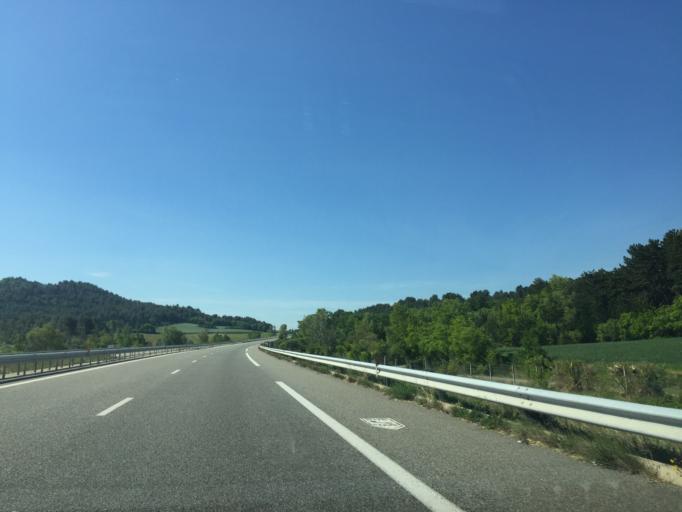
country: FR
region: Provence-Alpes-Cote d'Azur
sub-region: Departement des Alpes-de-Haute-Provence
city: Volonne
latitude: 44.1015
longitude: 5.9945
